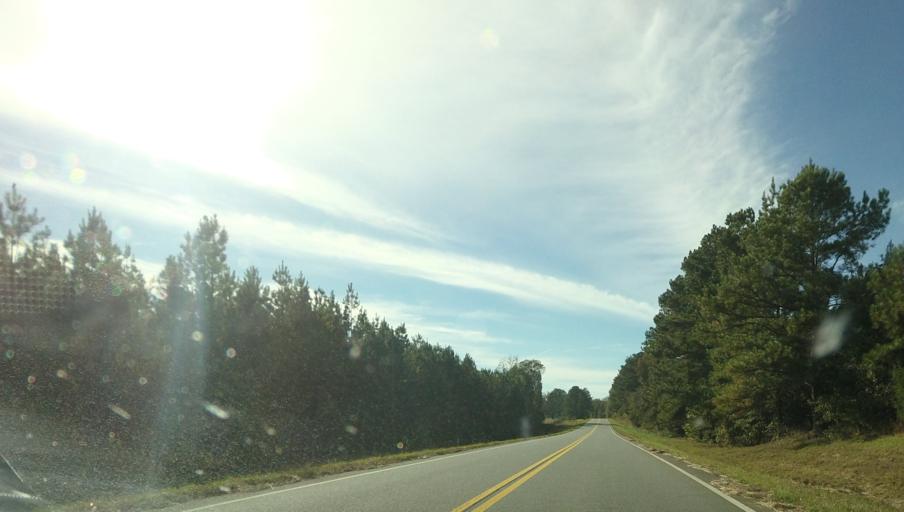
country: US
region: Georgia
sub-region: Talbot County
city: Talbotton
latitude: 32.7124
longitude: -84.3657
